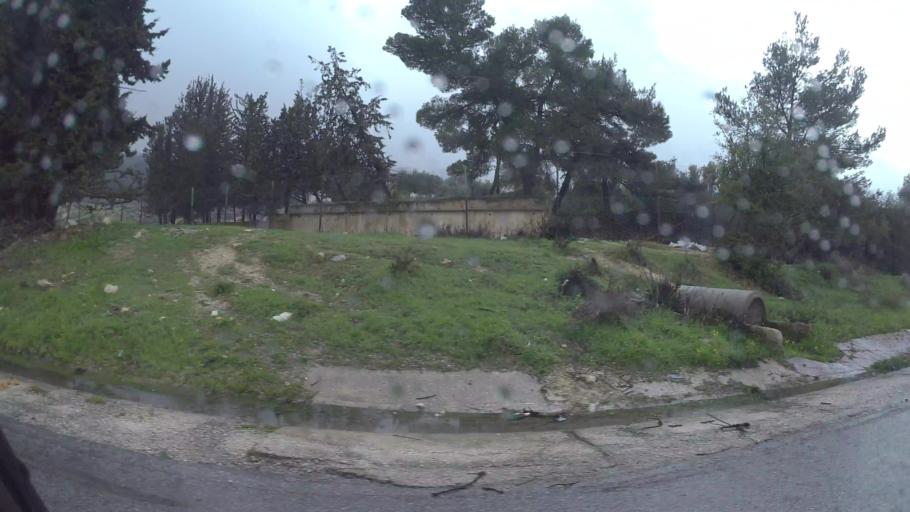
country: JO
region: Amman
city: Al Jubayhah
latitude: 32.0144
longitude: 35.8045
